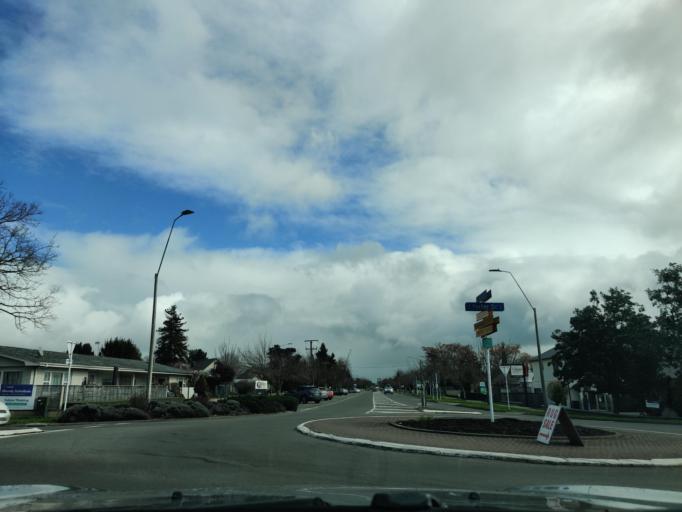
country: NZ
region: Hawke's Bay
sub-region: Hastings District
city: Hastings
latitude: -39.6705
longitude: 176.8760
